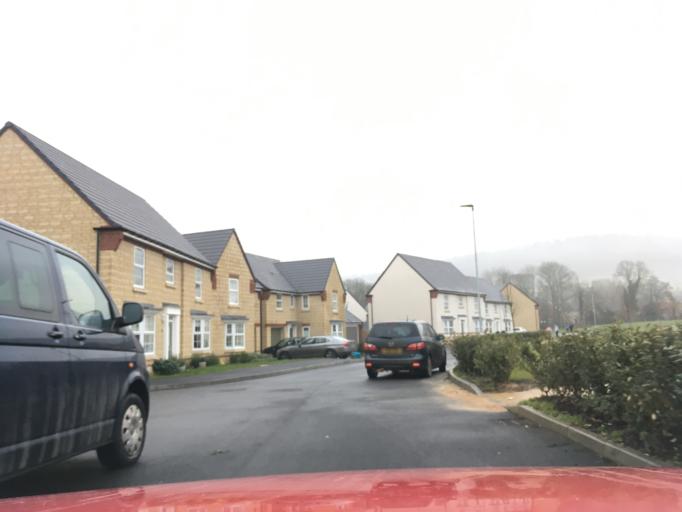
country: GB
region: England
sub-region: Gloucestershire
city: Stonehouse
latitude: 51.7292
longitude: -2.2797
